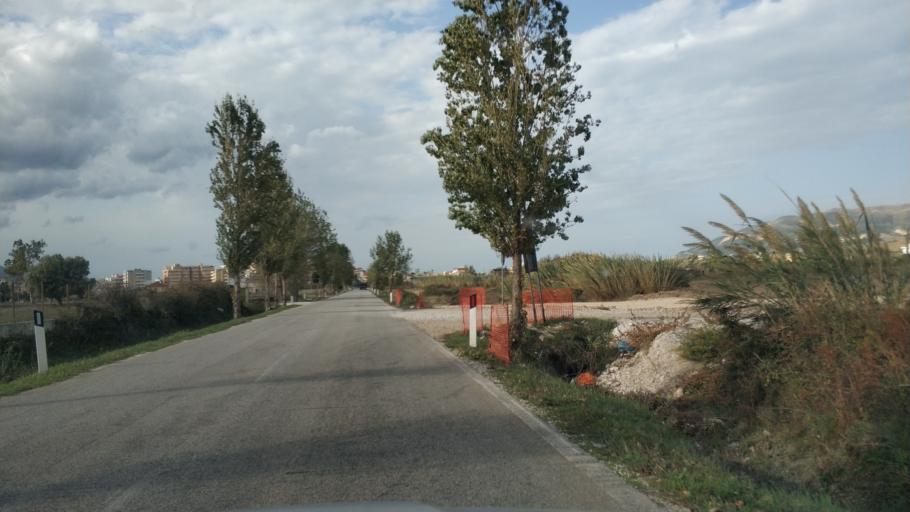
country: AL
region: Vlore
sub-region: Rrethi i Vlores
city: Orikum
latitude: 40.3230
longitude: 19.4808
